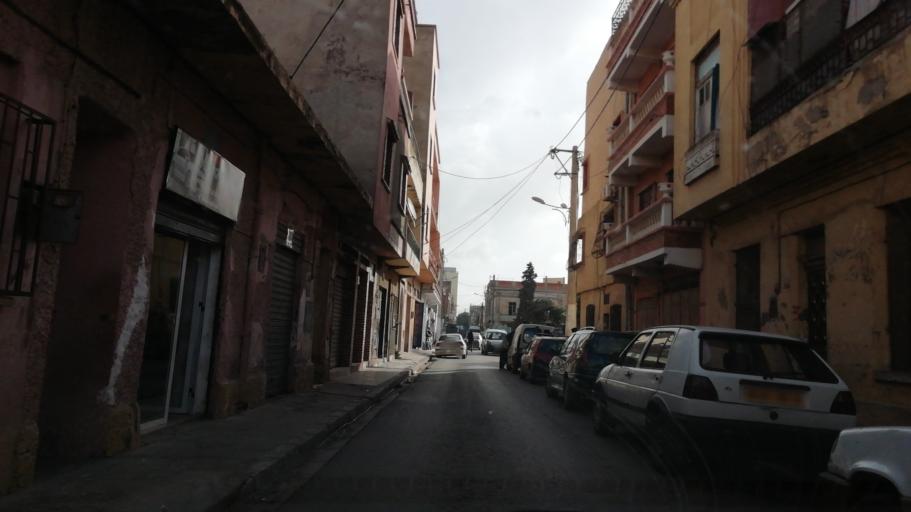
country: DZ
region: Oran
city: Oran
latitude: 35.6955
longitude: -0.6247
